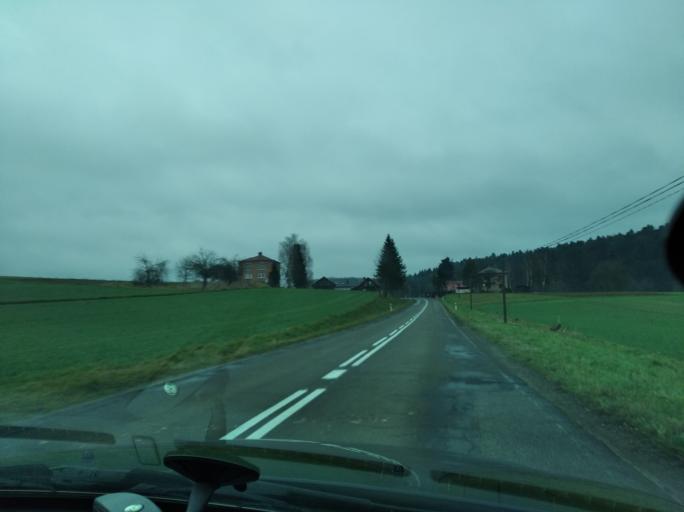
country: PL
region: Subcarpathian Voivodeship
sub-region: Powiat rzeszowski
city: Dynow
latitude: 49.8548
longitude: 22.2492
